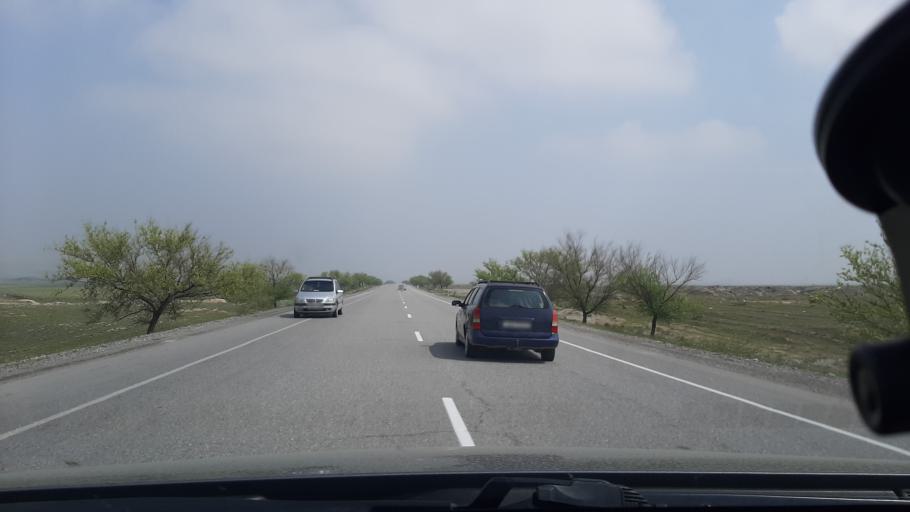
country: UZ
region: Toshkent
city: Bekobod
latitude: 40.1043
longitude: 69.1808
